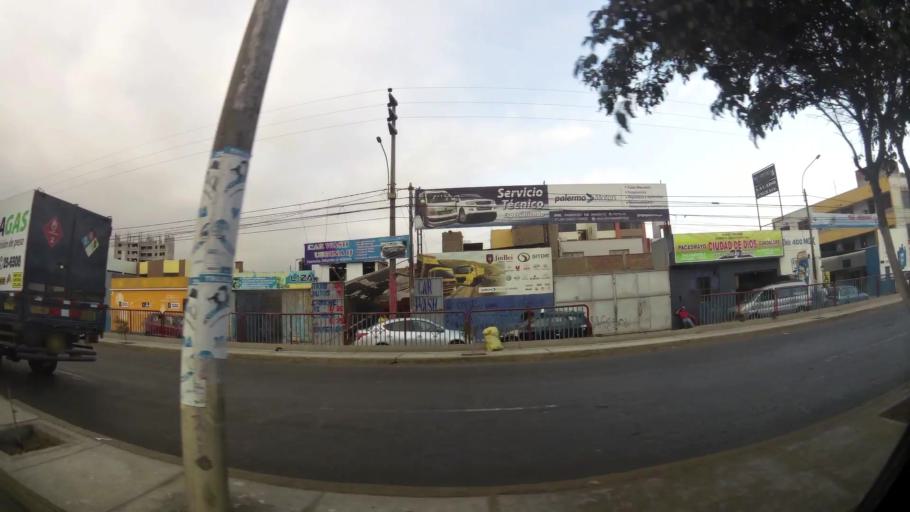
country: PE
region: La Libertad
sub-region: Provincia de Trujillo
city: Trujillo
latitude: -8.0989
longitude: -79.0374
